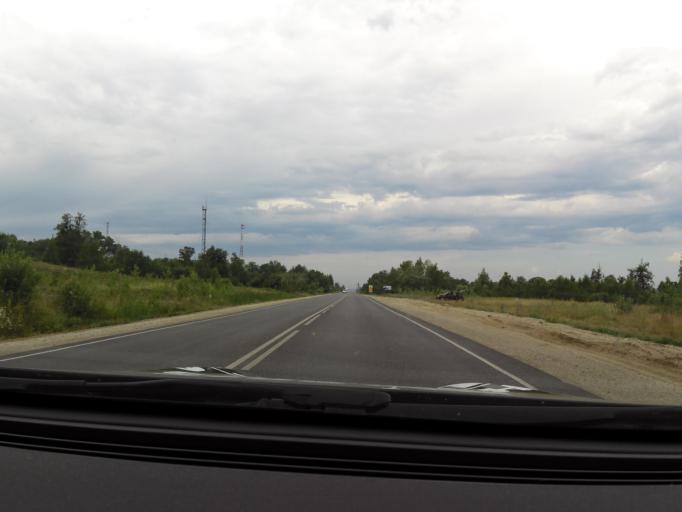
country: RU
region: Bashkortostan
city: Ulu-Telyak
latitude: 54.8430
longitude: 57.0686
